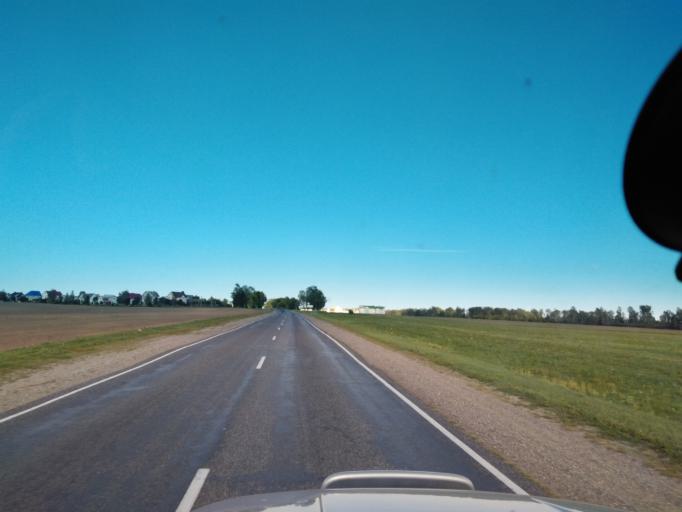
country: BY
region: Minsk
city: Dzyarzhynsk
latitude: 53.6698
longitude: 27.1067
